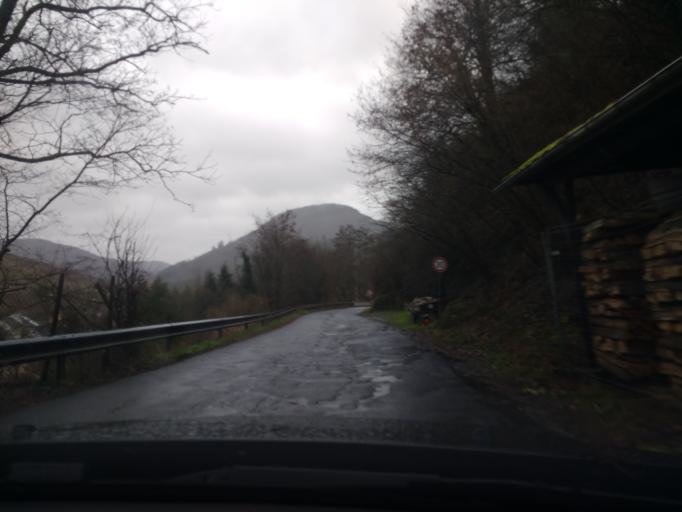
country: DE
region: Rheinland-Pfalz
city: Enkirch
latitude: 49.9830
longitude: 7.1317
